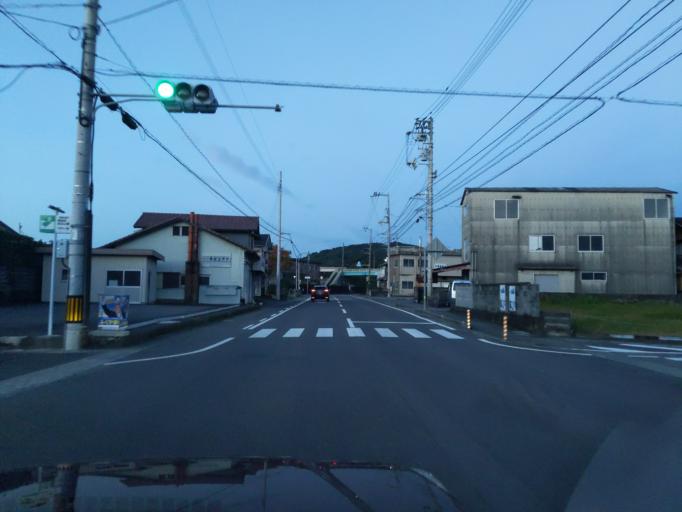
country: JP
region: Tokushima
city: Anan
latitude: 33.8727
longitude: 134.6420
